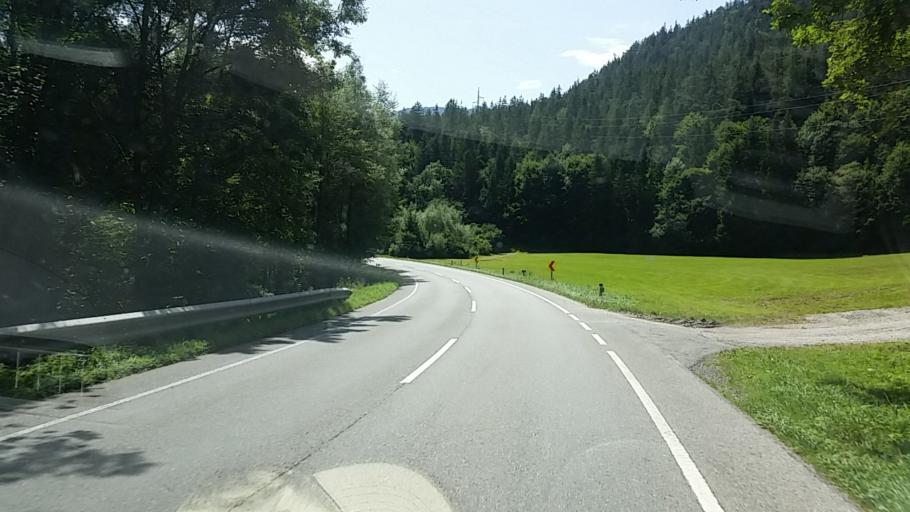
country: AT
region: Salzburg
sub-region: Politischer Bezirk Sankt Johann im Pongau
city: Werfen
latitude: 47.5076
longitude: 13.1665
